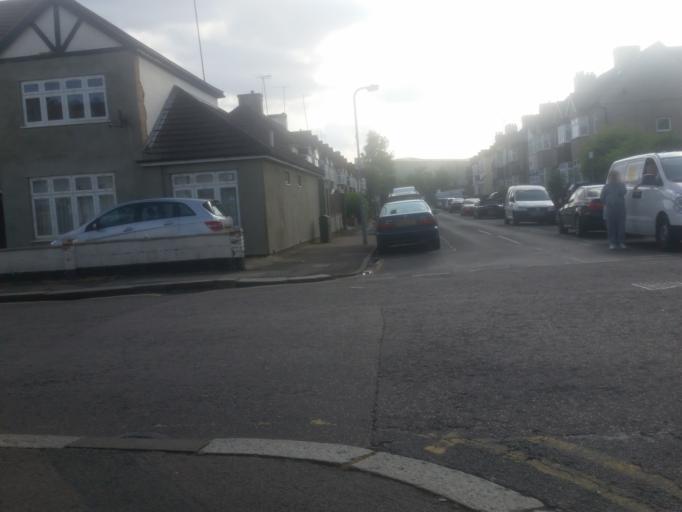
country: GB
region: England
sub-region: Hertfordshire
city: Borehamwood
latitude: 51.6577
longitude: -0.2759
